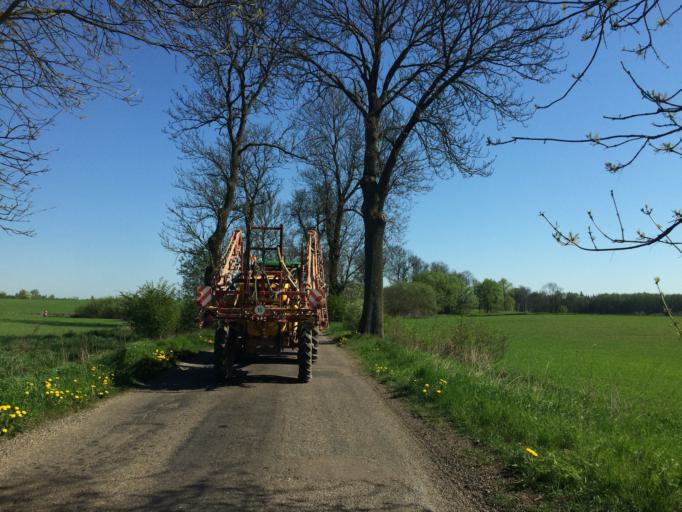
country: PL
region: Warmian-Masurian Voivodeship
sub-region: Powiat ostrodzki
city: Dabrowno
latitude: 53.4705
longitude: 19.9664
